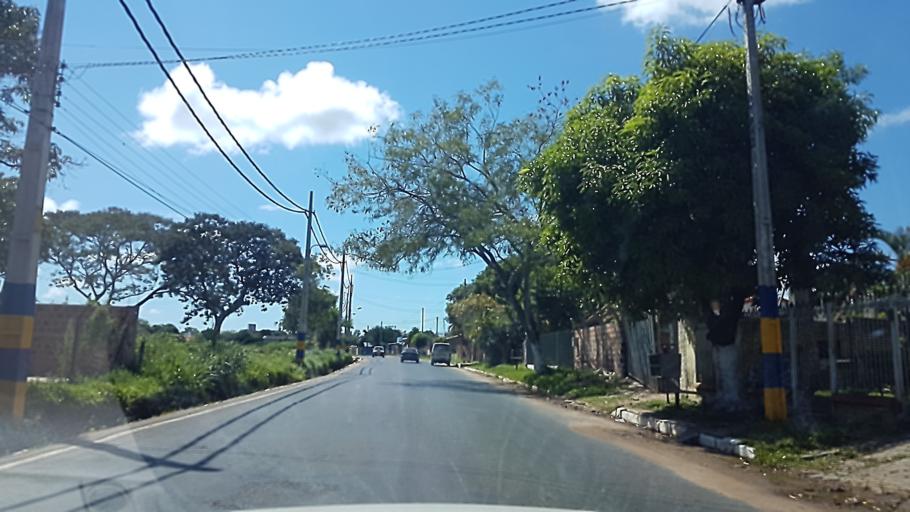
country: PY
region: Central
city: San Lorenzo
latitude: -25.2792
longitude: -57.4948
